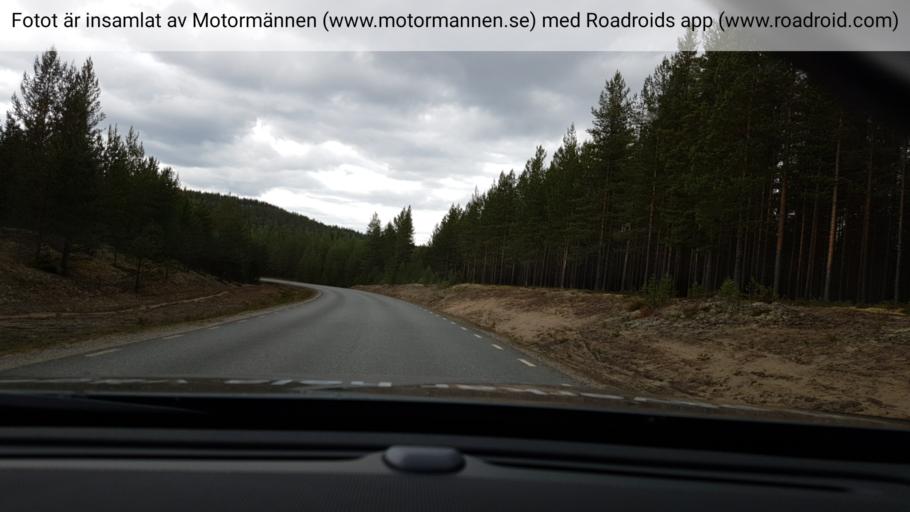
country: SE
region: Vaesterbotten
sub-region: Vindelns Kommun
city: Vindeln
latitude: 64.1787
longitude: 19.6504
